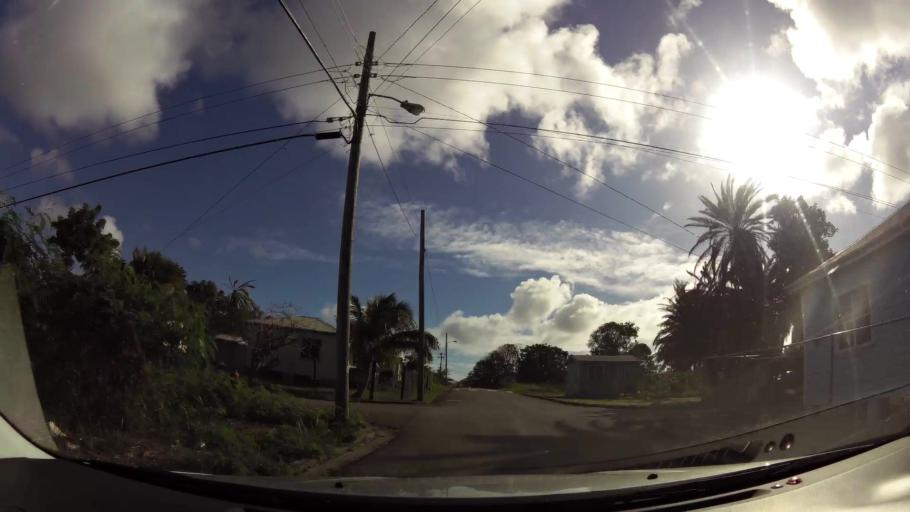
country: AG
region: Saint Peter
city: All Saints
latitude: 17.0676
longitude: -61.7910
